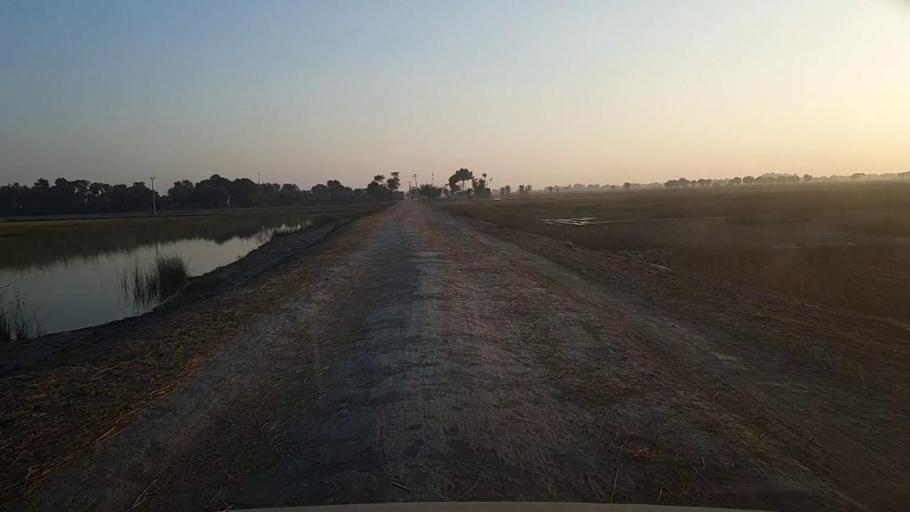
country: PK
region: Sindh
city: Khairpur Nathan Shah
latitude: 27.1728
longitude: 67.7333
